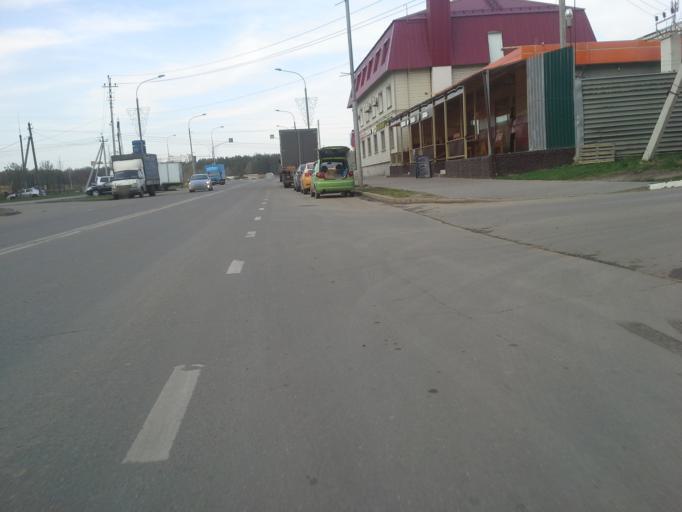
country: RU
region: Moskovskaya
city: Kommunarka
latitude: 55.5706
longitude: 37.4932
